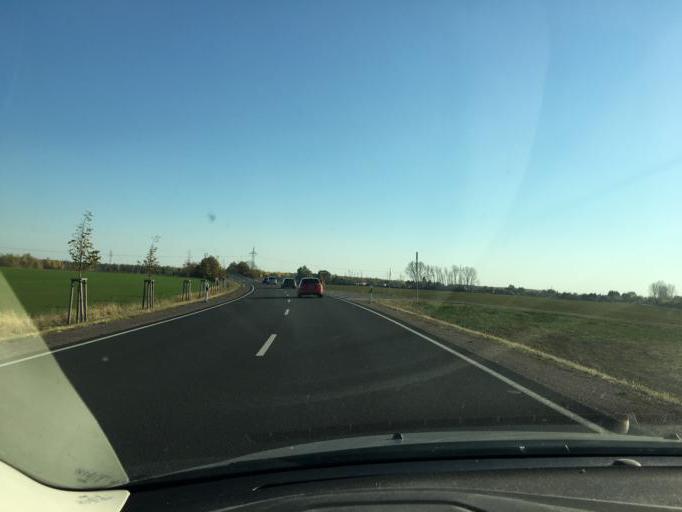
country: DE
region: Saxony-Anhalt
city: Roitzsch
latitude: 51.5874
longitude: 12.2787
